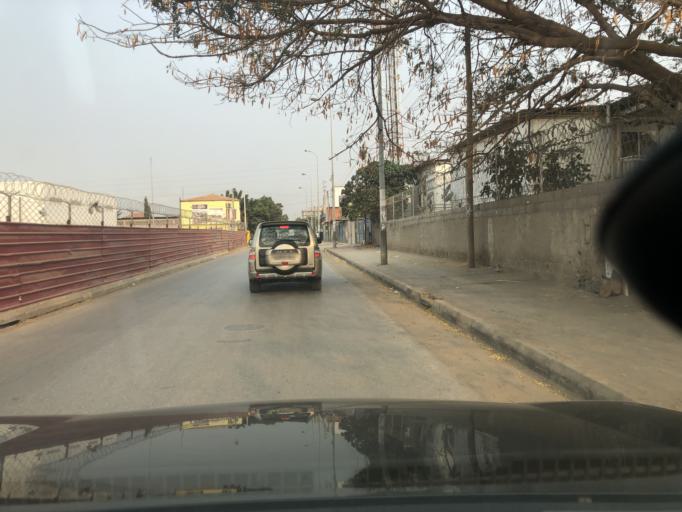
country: AO
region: Luanda
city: Luanda
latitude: -8.8800
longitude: 13.1959
